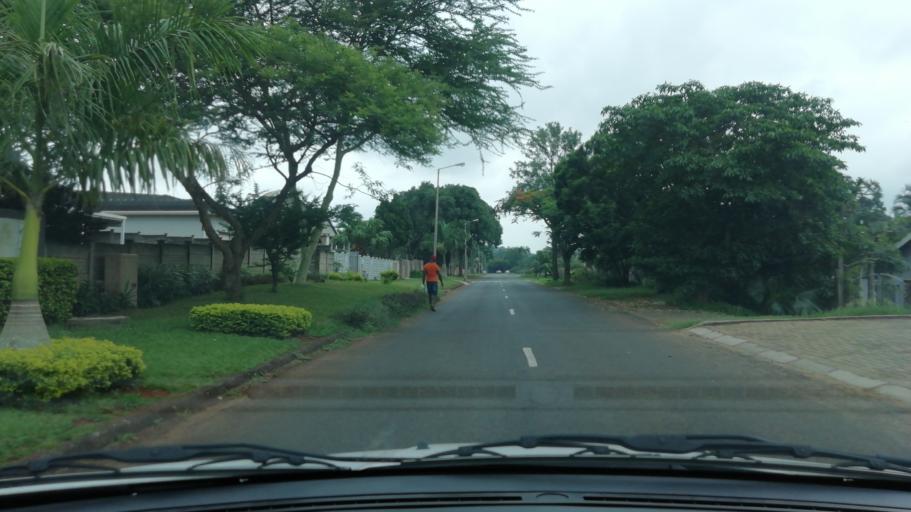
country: ZA
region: KwaZulu-Natal
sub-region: uThungulu District Municipality
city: Empangeni
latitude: -28.7623
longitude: 31.8992
